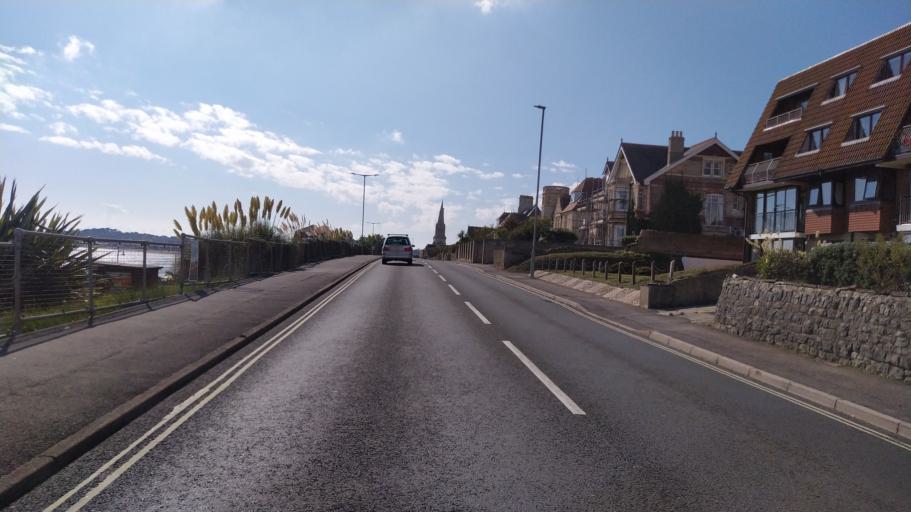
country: GB
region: England
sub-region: Dorset
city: Weymouth
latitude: 50.6218
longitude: -2.4476
